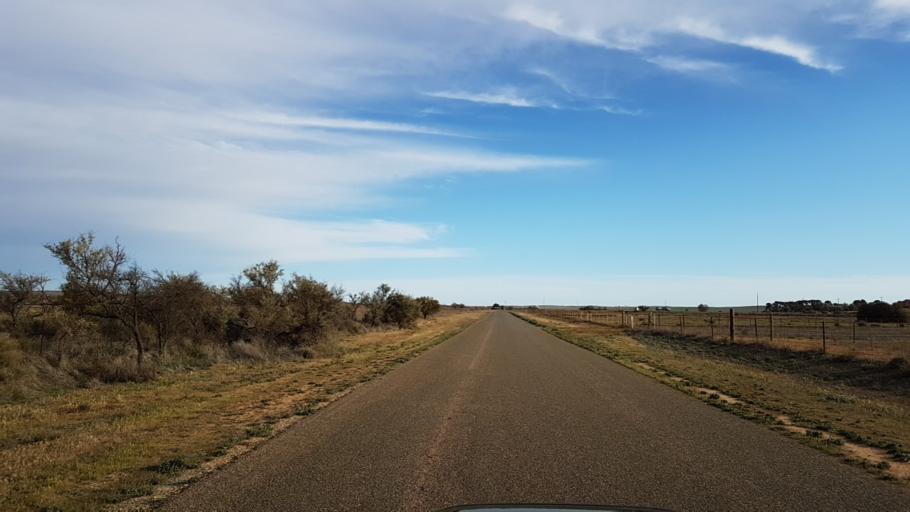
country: AU
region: South Australia
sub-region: Peterborough
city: Peterborough
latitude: -32.9870
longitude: 138.8501
